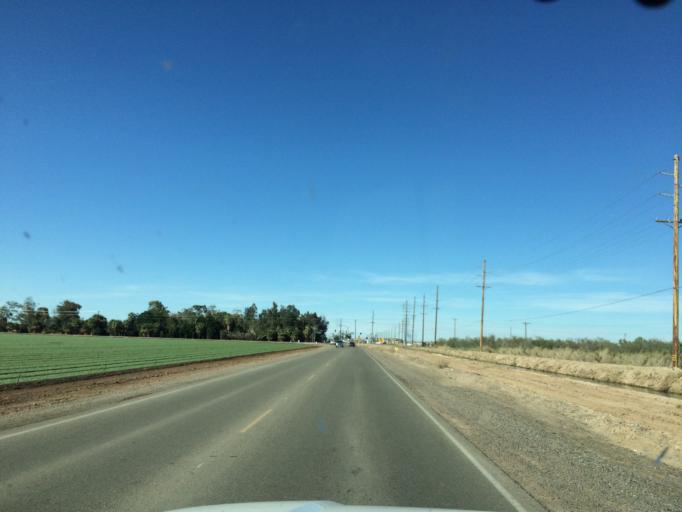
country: US
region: California
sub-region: Imperial County
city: Heber
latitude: 32.7493
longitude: -115.5347
